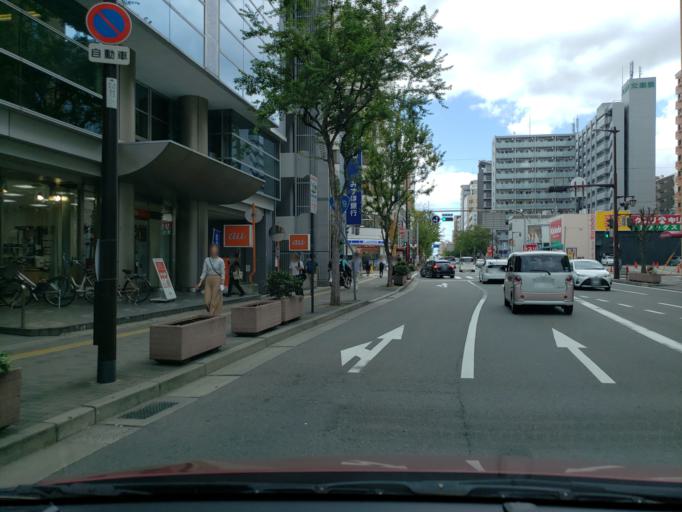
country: JP
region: Osaka
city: Suita
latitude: 34.7576
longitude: 135.4975
